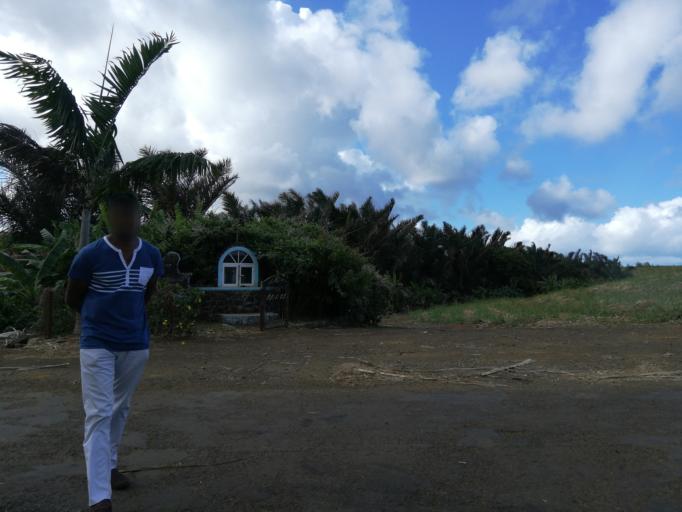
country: MU
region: Flacq
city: Bel Air Riviere Seche
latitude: -20.2798
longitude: 57.7444
